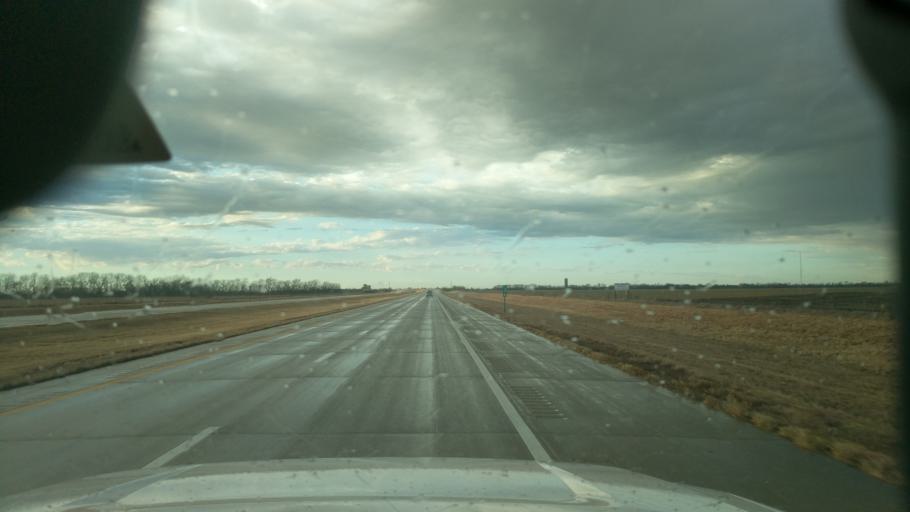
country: US
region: Kansas
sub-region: Harvey County
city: North Newton
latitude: 38.0945
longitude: -97.3630
